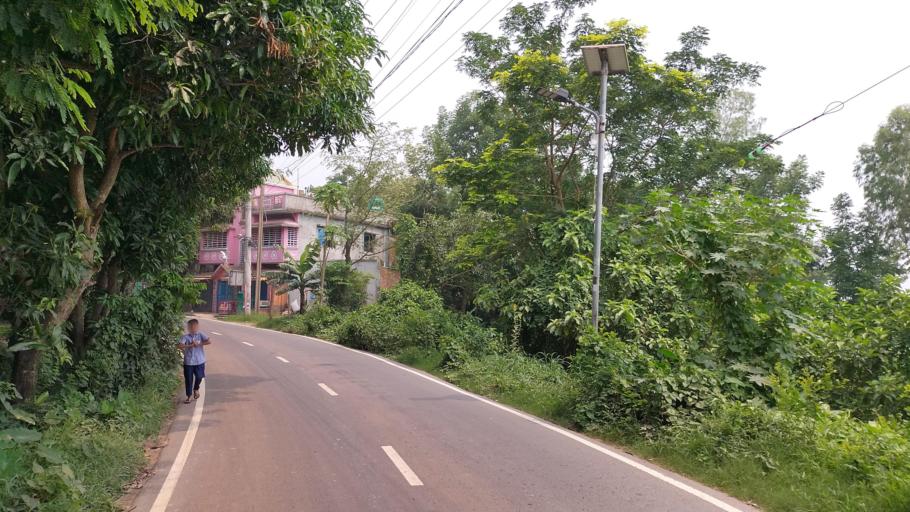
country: BD
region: Dhaka
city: Azimpur
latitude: 23.7209
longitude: 90.2751
